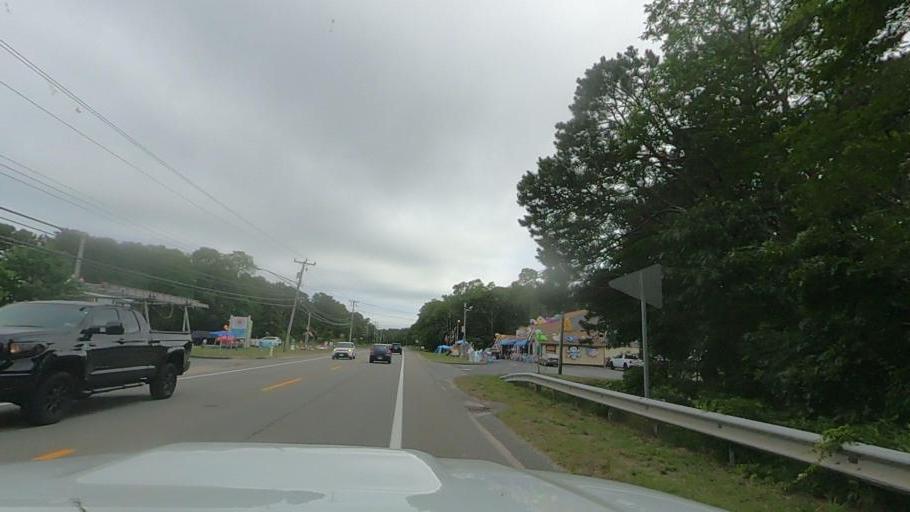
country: US
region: Massachusetts
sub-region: Barnstable County
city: North Eastham
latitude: 41.8905
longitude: -69.9880
